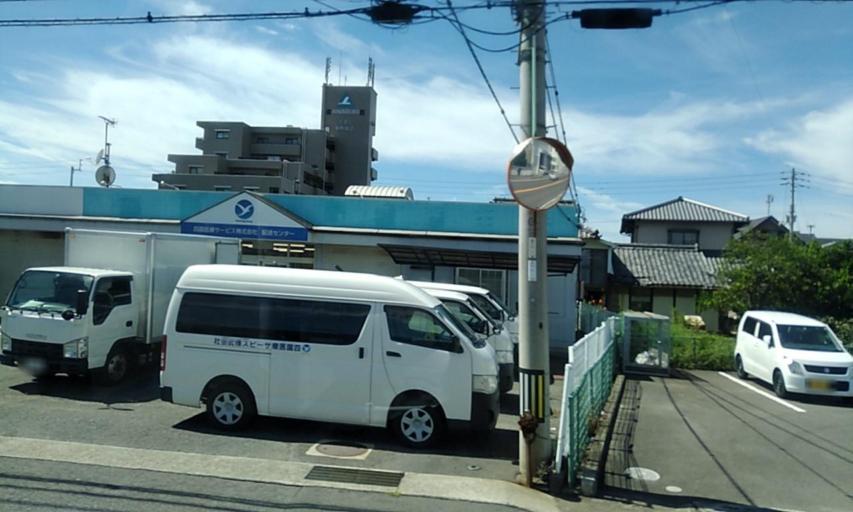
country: JP
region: Kagawa
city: Takamatsu-shi
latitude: 34.3079
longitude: 134.0707
